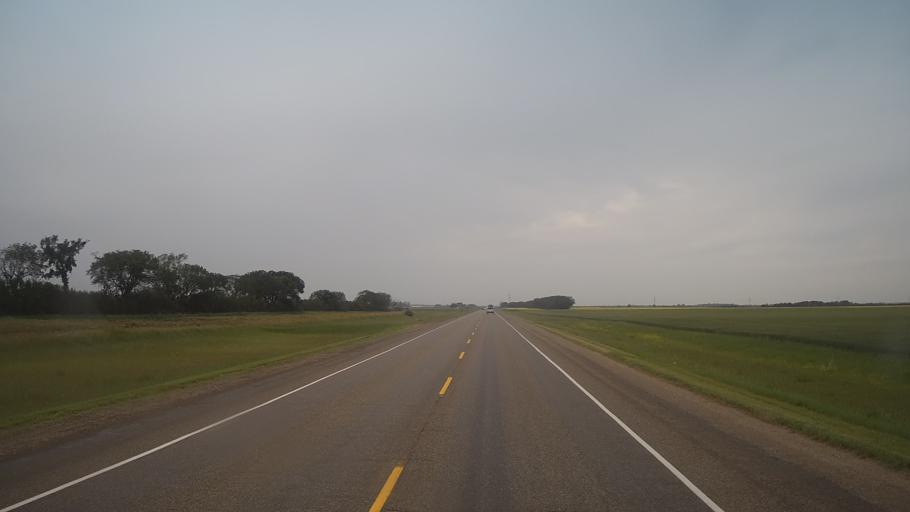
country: CA
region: Saskatchewan
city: Saskatoon
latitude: 52.1292
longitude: -106.8279
